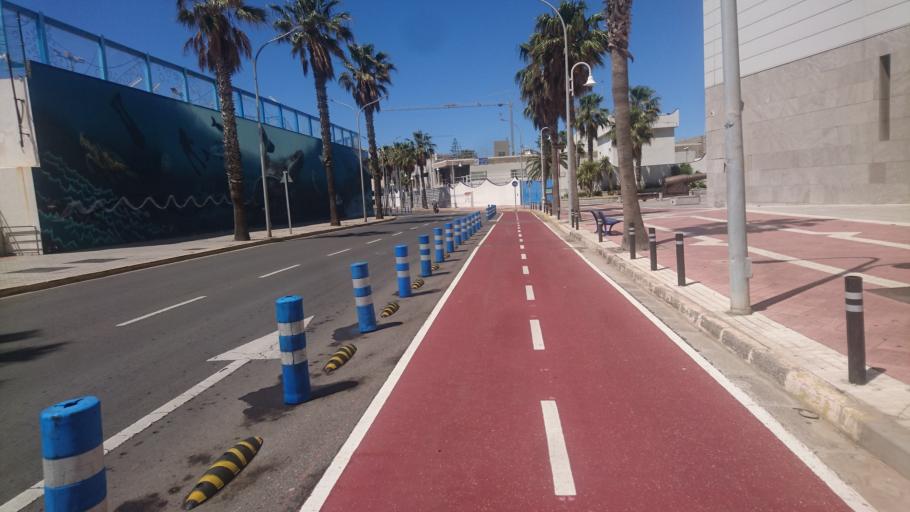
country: ES
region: Melilla
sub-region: Melilla
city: Melilla
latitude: 35.2898
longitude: -2.9364
